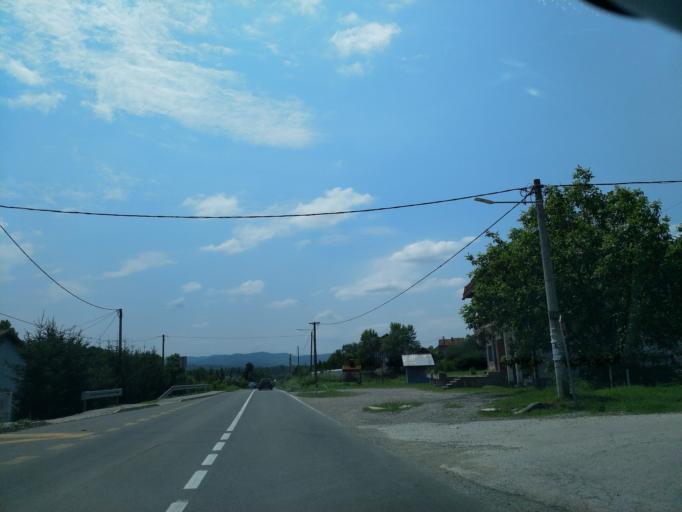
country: RS
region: Central Serbia
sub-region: Rasinski Okrug
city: Krusevac
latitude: 43.4894
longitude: 21.2794
